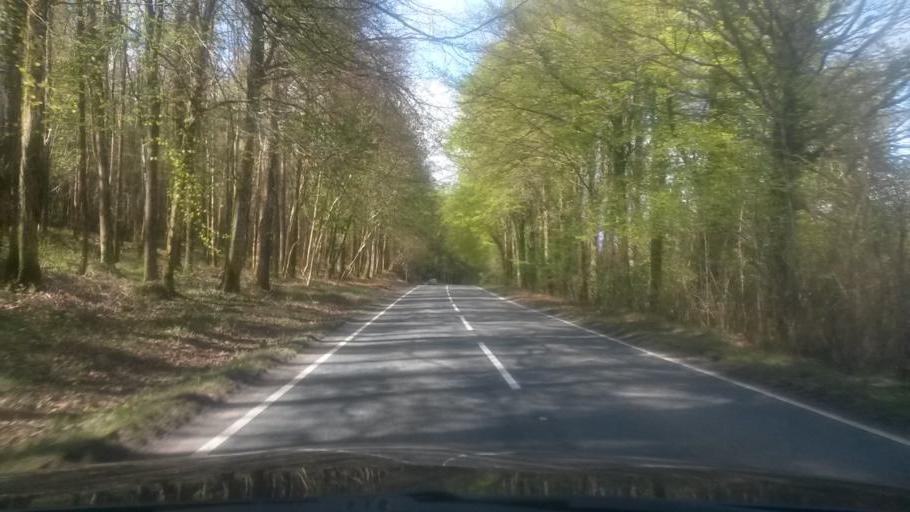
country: GB
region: Northern Ireland
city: Irvinestown
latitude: 54.4136
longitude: -7.7269
